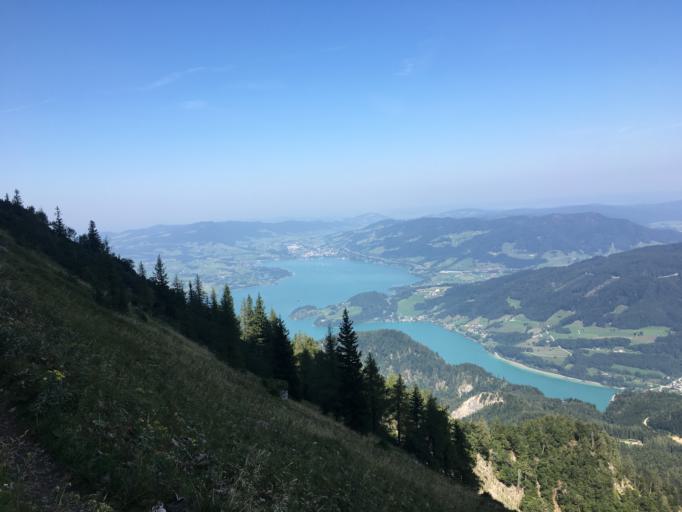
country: AT
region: Upper Austria
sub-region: Politischer Bezirk Gmunden
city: Sankt Wolfgang im Salzkammergut
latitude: 47.7777
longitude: 13.4328
